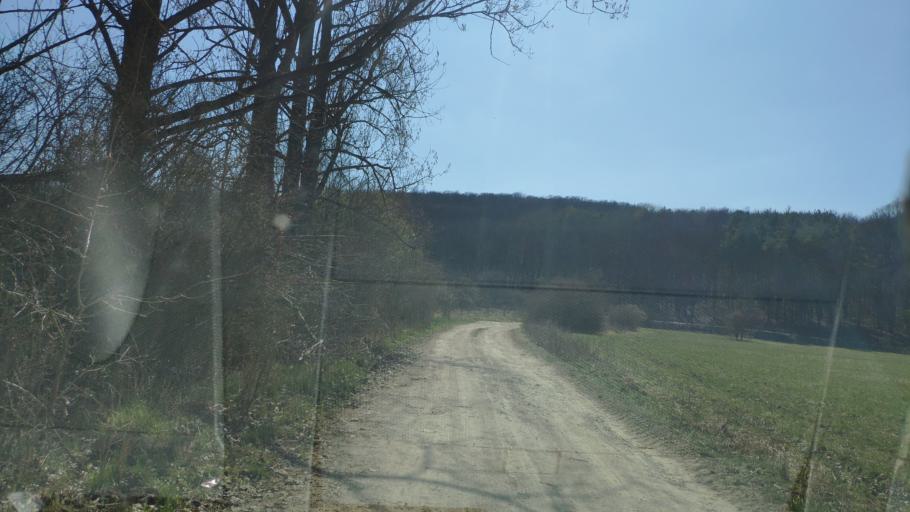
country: SK
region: Kosicky
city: Moldava nad Bodvou
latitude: 48.5673
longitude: 20.9428
